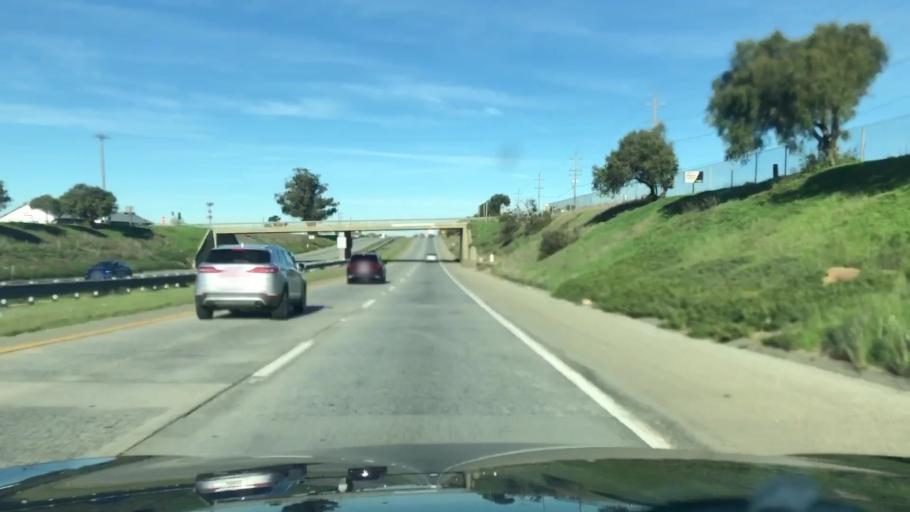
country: US
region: California
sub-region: Monterey County
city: Chualar
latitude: 36.5689
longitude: -121.5170
